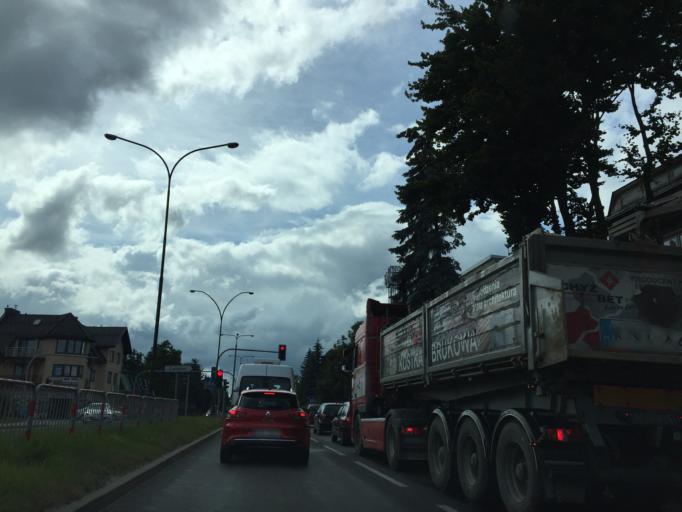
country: PL
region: Lesser Poland Voivodeship
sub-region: Powiat nowotarski
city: Nowy Targ
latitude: 49.4775
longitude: 20.0331
